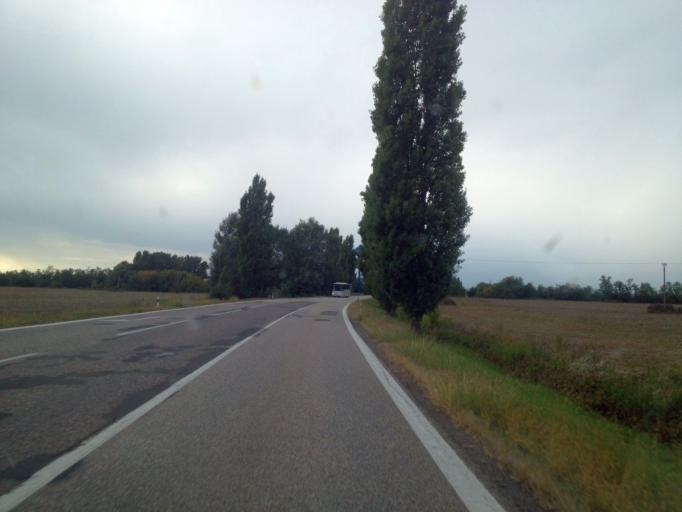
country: HU
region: Komarom-Esztergom
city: Sutto
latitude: 47.7696
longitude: 18.4746
